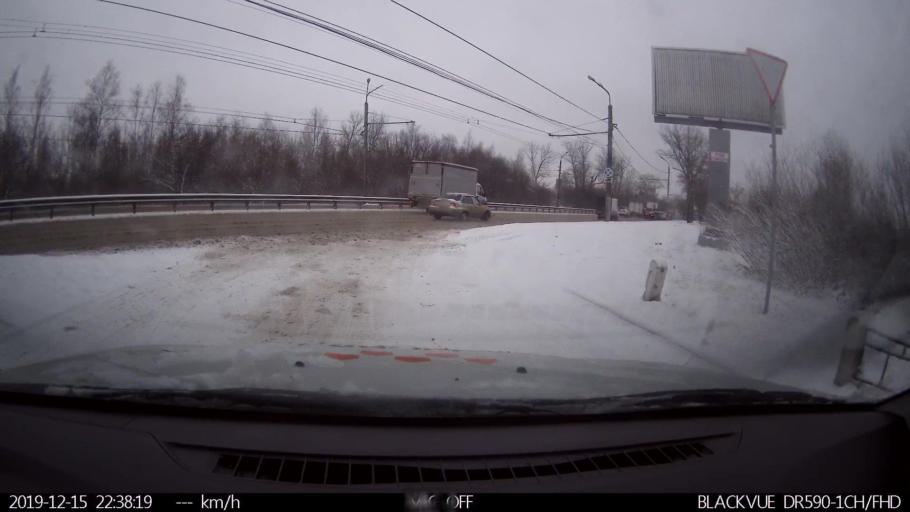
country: RU
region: Nizjnij Novgorod
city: Gorbatovka
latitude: 56.3120
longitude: 43.8351
